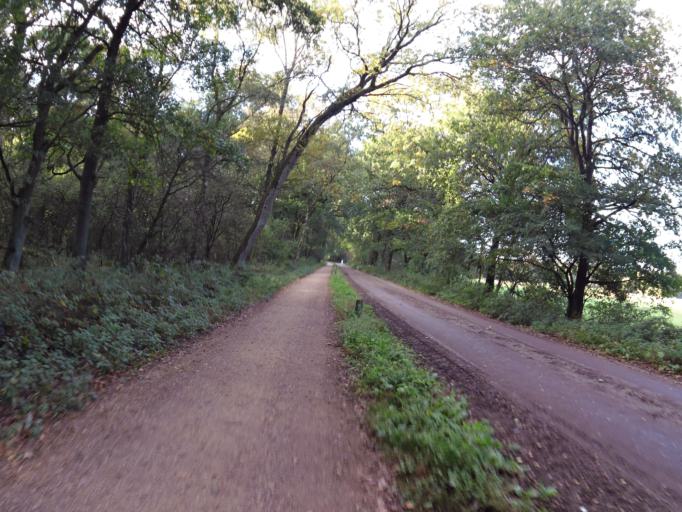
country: NL
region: Limburg
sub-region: Gemeente Bergen
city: Wellerlooi
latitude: 51.5621
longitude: 6.1120
